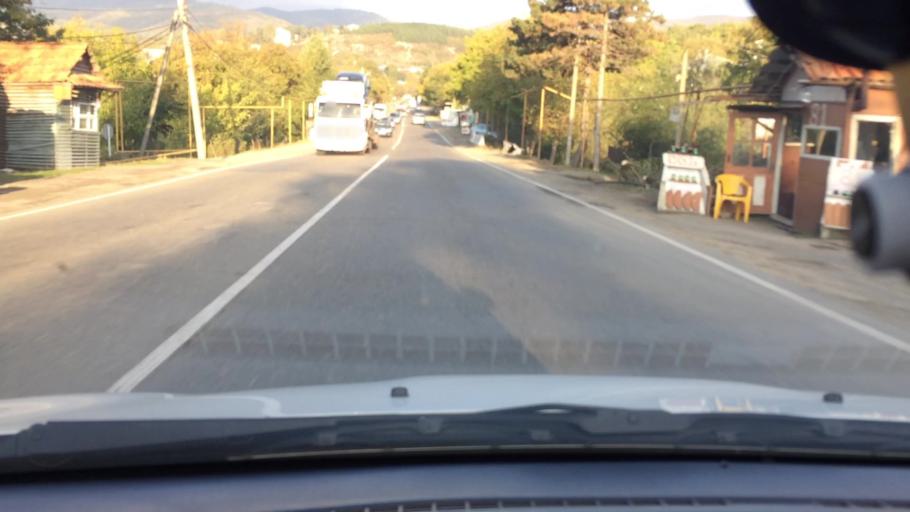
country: GE
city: Surami
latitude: 42.0283
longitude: 43.5536
